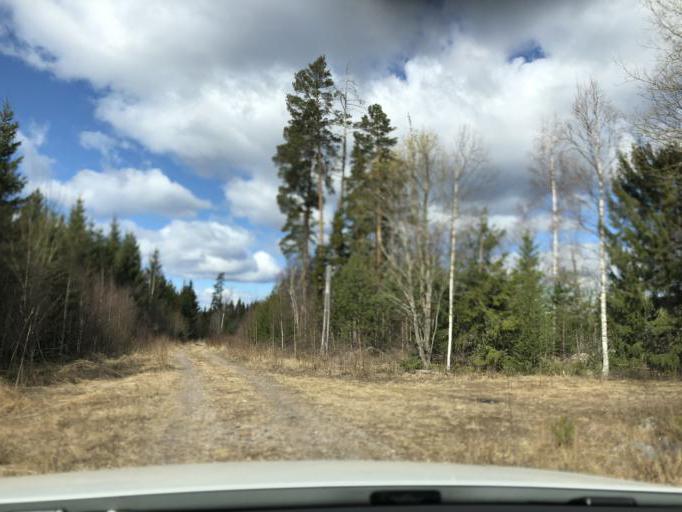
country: SE
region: Uppsala
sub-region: Tierps Kommun
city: Tierp
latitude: 60.3313
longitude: 17.3380
